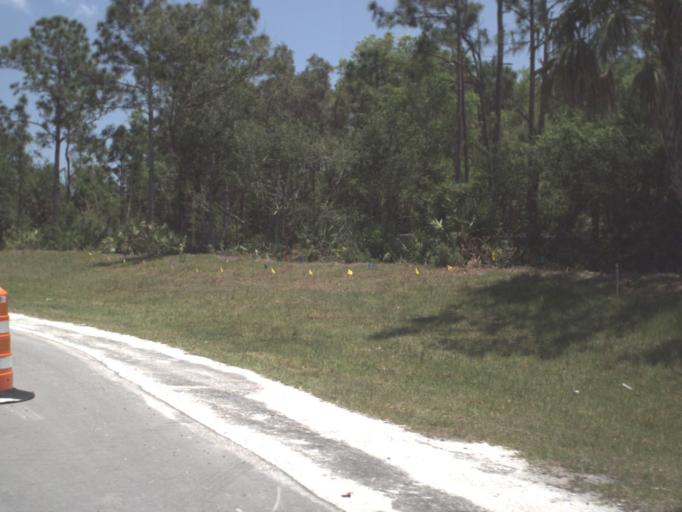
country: US
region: Florida
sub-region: Saint Lucie County
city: White City
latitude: 27.3743
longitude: -80.3686
